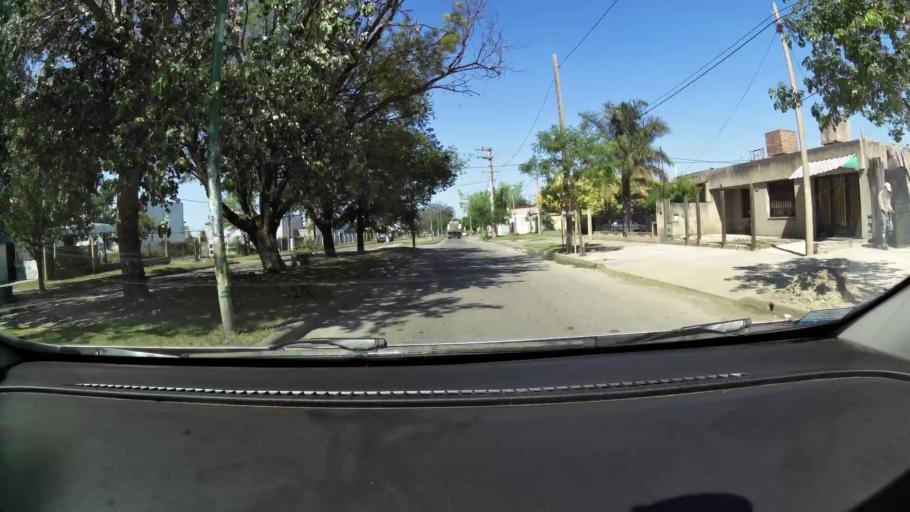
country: AR
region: Cordoba
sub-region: Departamento de Capital
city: Cordoba
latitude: -31.3669
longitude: -64.1554
